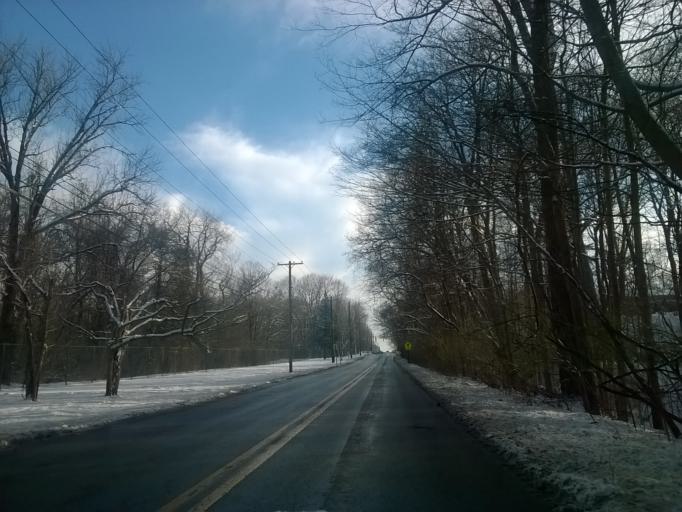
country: US
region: Indiana
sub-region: Marion County
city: Meridian Hills
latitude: 39.8925
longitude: -86.1459
